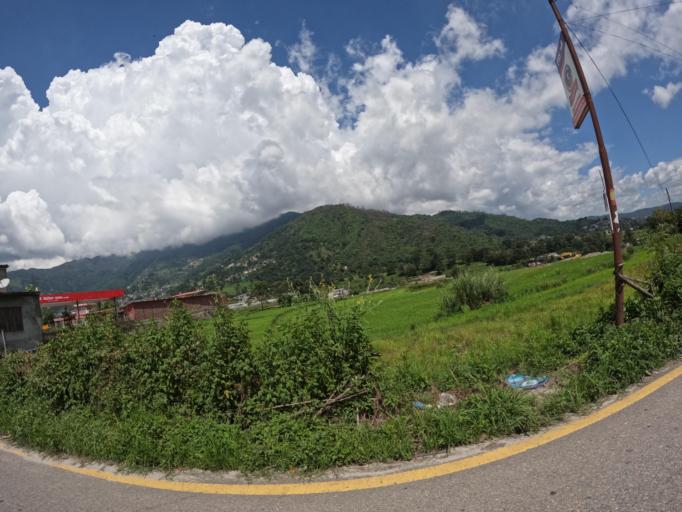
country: NP
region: Central Region
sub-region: Bagmati Zone
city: Kathmandu
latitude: 27.7810
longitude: 85.3250
